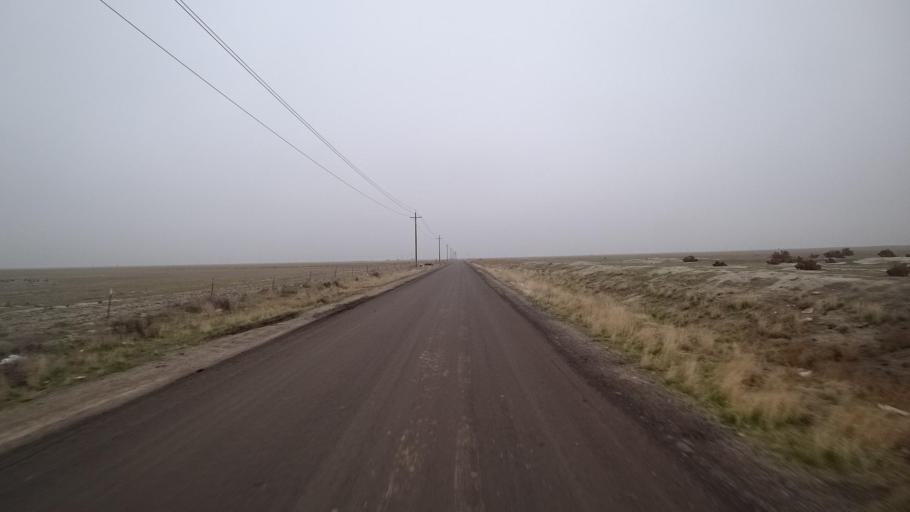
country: US
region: California
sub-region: Tulare County
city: Alpaugh
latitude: 35.7832
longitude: -119.4723
